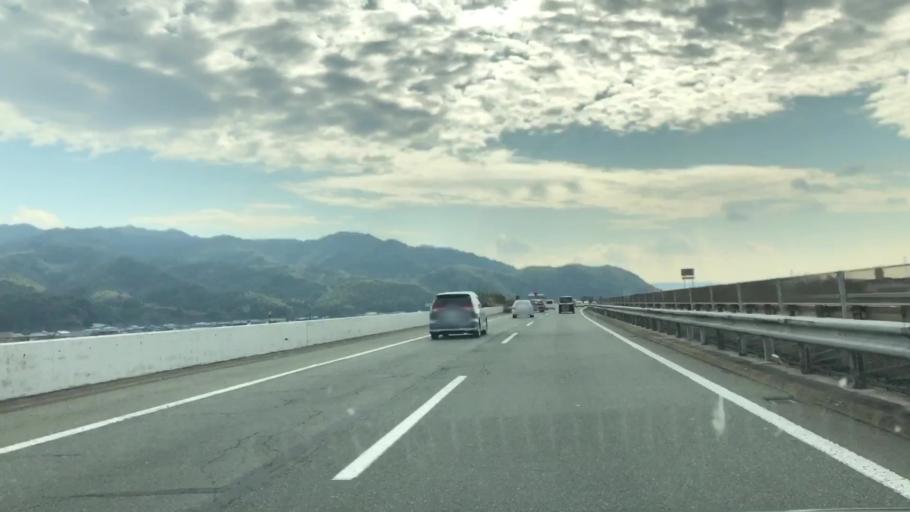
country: JP
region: Fukuoka
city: Setakamachi-takayanagi
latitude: 33.1810
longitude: 130.5180
